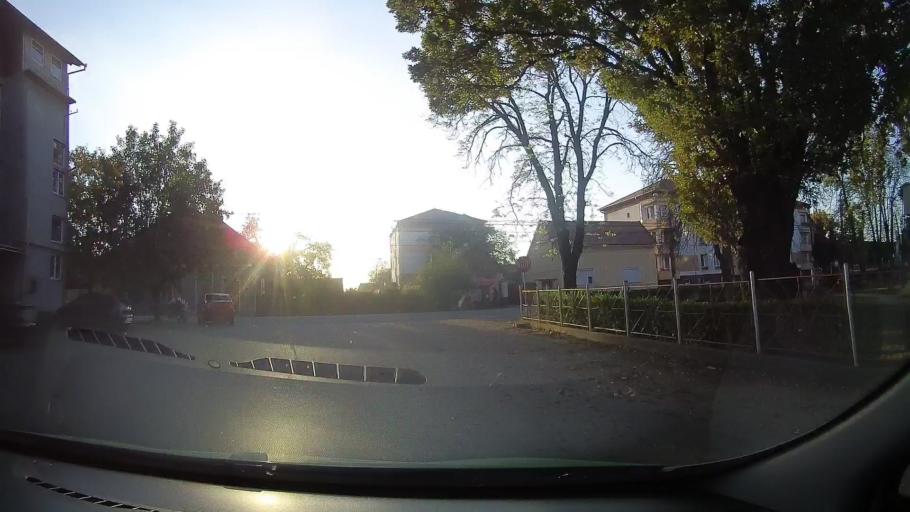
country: RO
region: Bihor
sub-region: Comuna Salard
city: Salard
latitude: 47.2252
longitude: 22.0284
